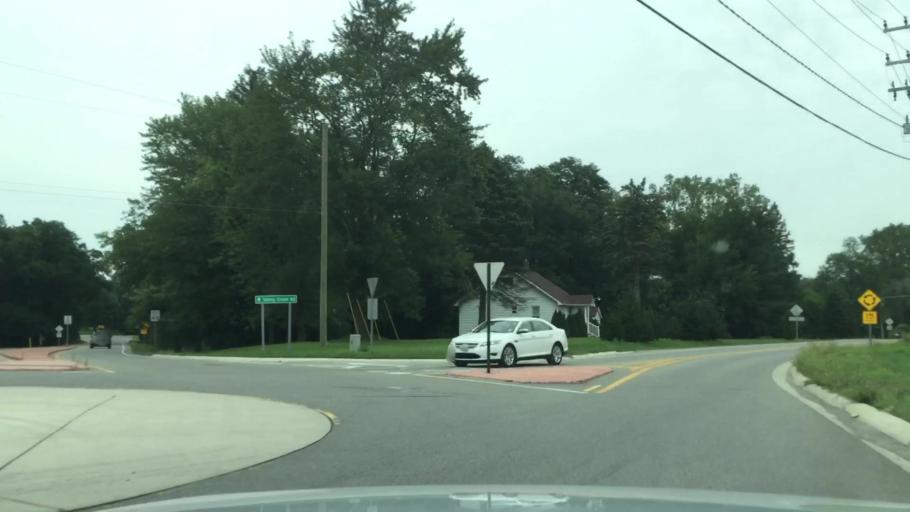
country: US
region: Michigan
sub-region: Washtenaw County
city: Ypsilanti
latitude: 42.2017
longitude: -83.6231
